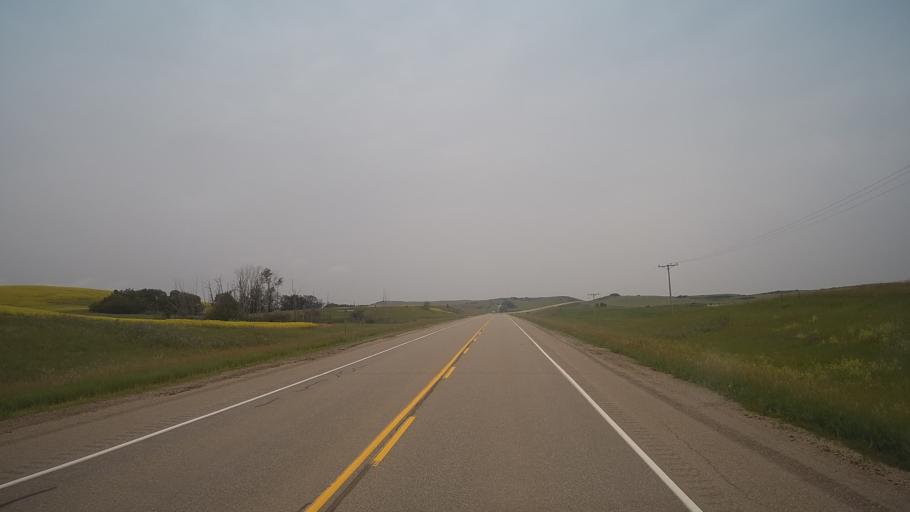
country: CA
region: Saskatchewan
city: Biggar
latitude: 52.0564
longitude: -107.8619
